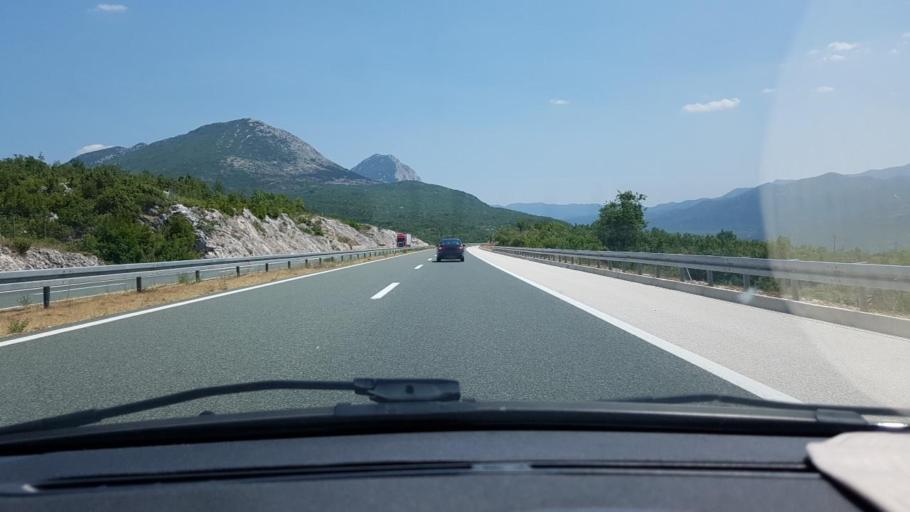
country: HR
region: Splitsko-Dalmatinska
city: Runovic
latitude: 43.3122
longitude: 17.1845
